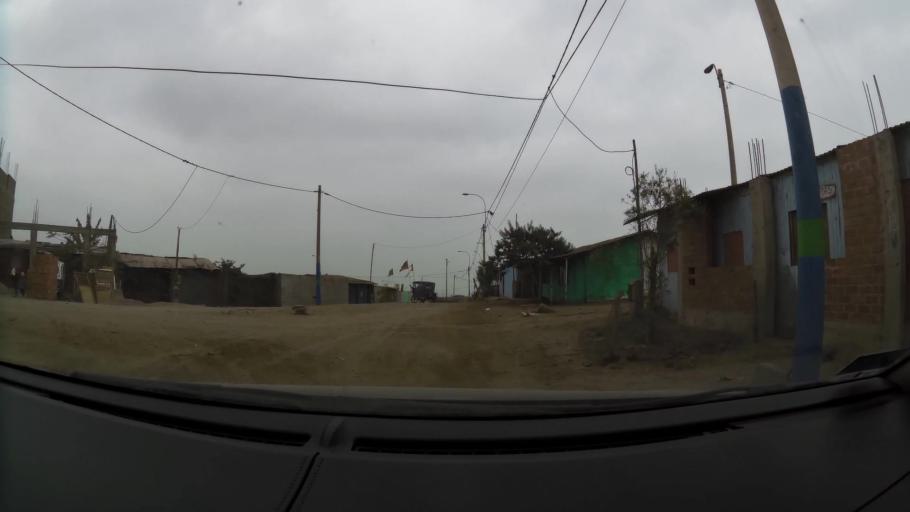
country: PE
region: Lima
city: Ventanilla
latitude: -11.8506
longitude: -77.1337
